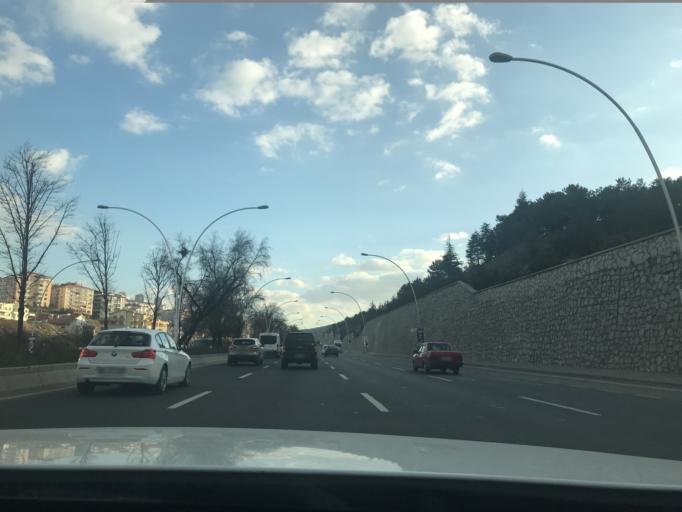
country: TR
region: Ankara
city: Ankara
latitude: 39.8780
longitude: 32.8114
